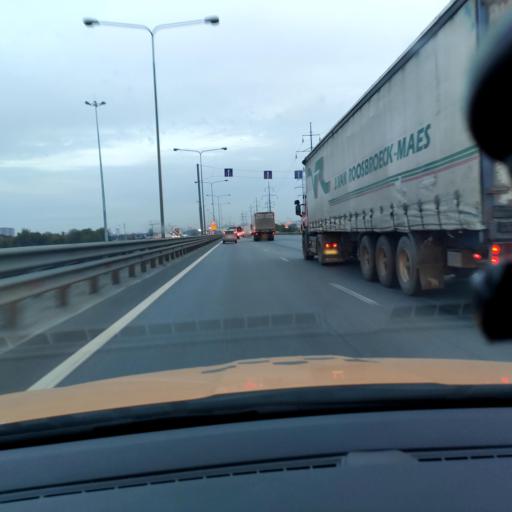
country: RU
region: Moskovskaya
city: Lyubertsy
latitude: 55.6479
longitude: 37.9126
